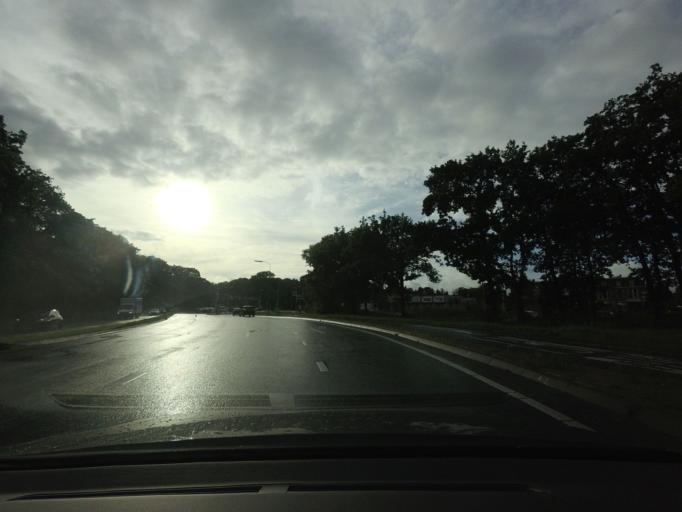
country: NL
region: South Holland
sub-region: Gemeente Wassenaar
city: Wassenaar
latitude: 52.1380
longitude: 4.4087
